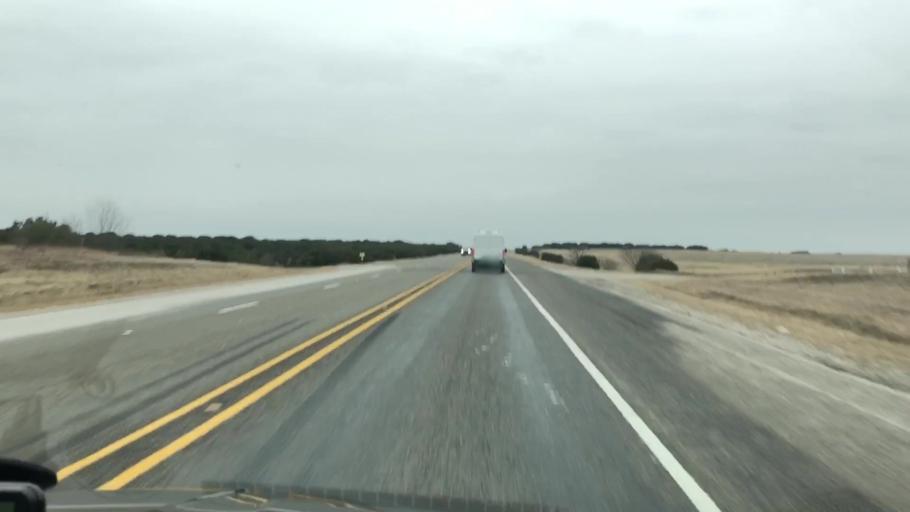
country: US
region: Texas
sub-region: Lampasas County
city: Lampasas
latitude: 31.1456
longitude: -98.1829
